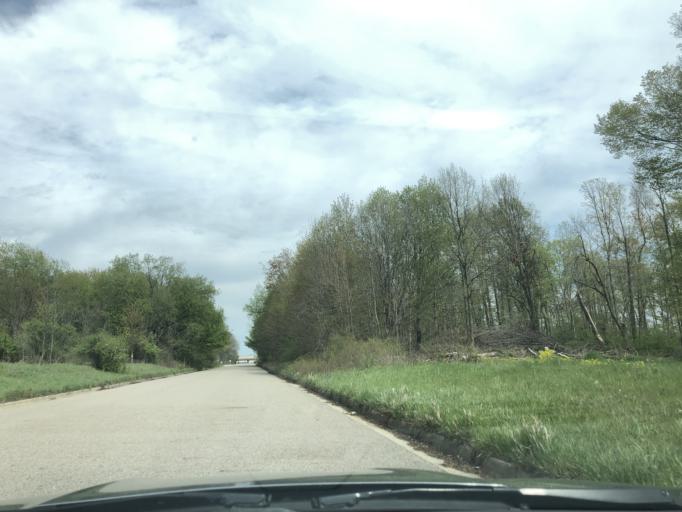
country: US
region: Michigan
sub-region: Eaton County
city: Waverly
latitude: 42.7078
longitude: -84.6493
